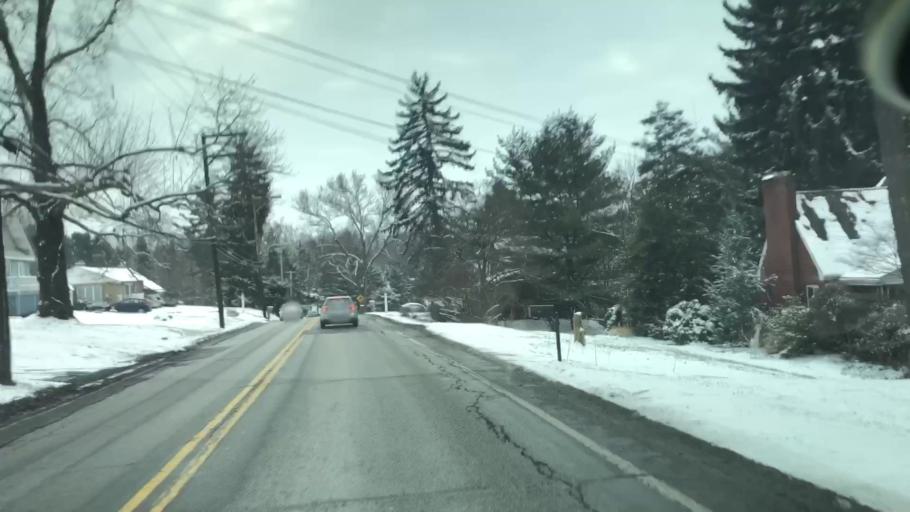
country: US
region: Pennsylvania
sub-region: Allegheny County
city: Monroeville
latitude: 40.4518
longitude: -79.7616
